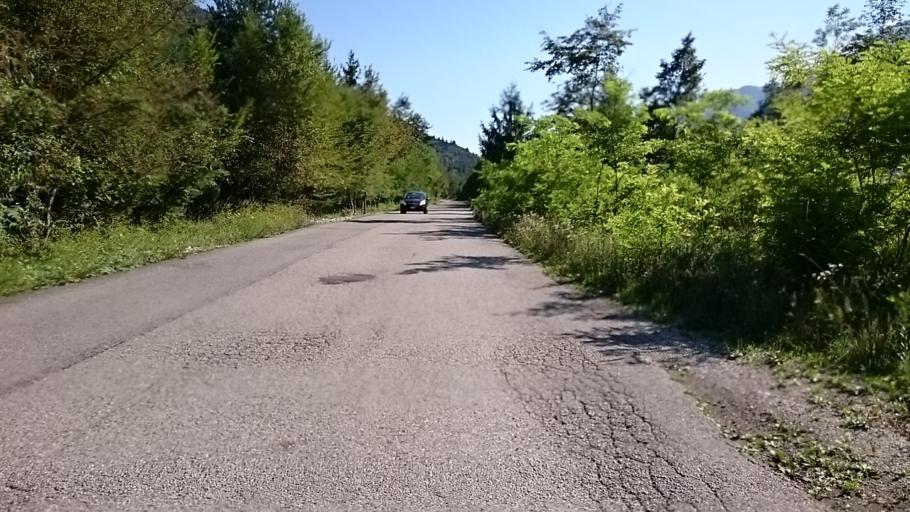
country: IT
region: Veneto
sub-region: Provincia di Belluno
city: Longarone
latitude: 46.2419
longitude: 12.3082
